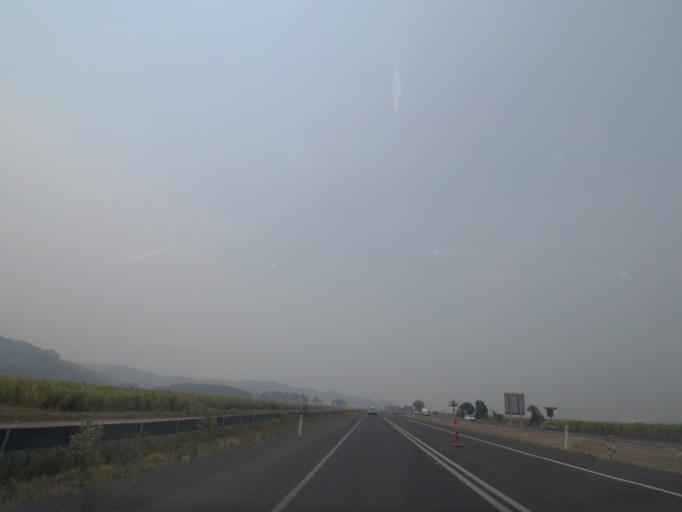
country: AU
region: New South Wales
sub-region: Ballina
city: Ballina
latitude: -28.8983
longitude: 153.4805
